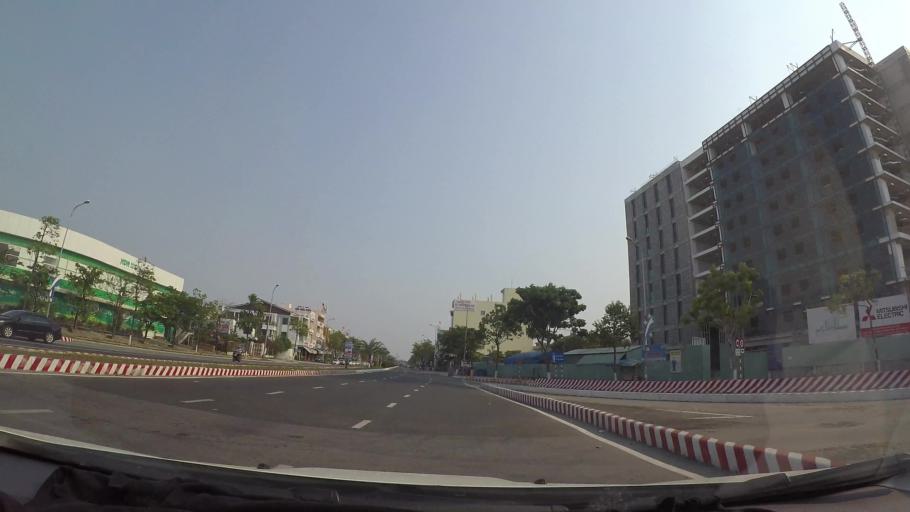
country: VN
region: Da Nang
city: Cam Le
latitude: 16.0243
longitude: 108.2090
